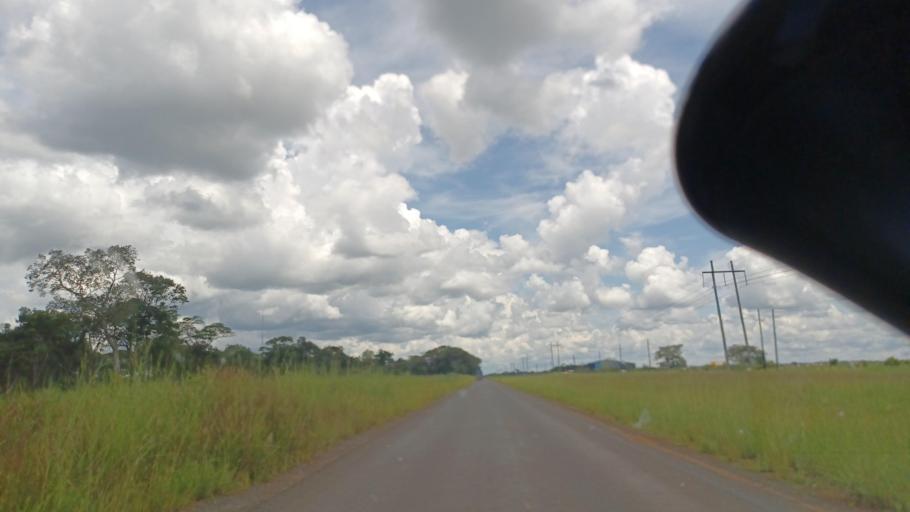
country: ZM
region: North-Western
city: Solwezi
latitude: -12.4443
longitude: 26.2078
